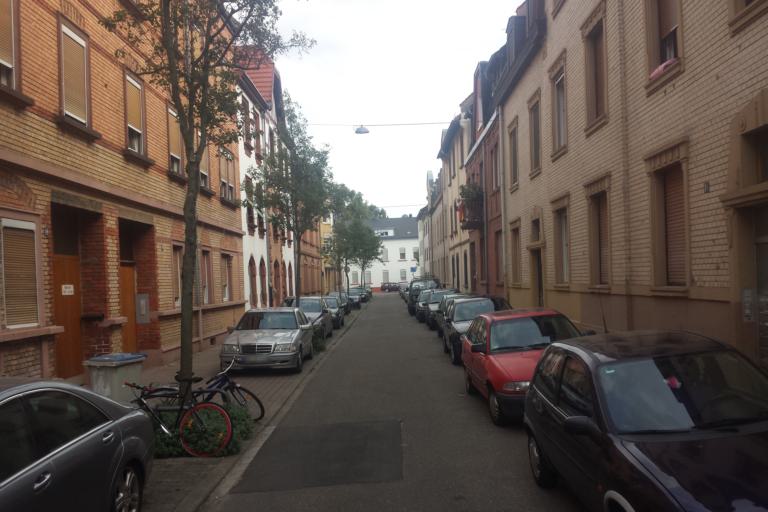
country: DE
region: Baden-Wuerttemberg
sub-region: Karlsruhe Region
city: Mannheim
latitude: 49.5261
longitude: 8.4785
